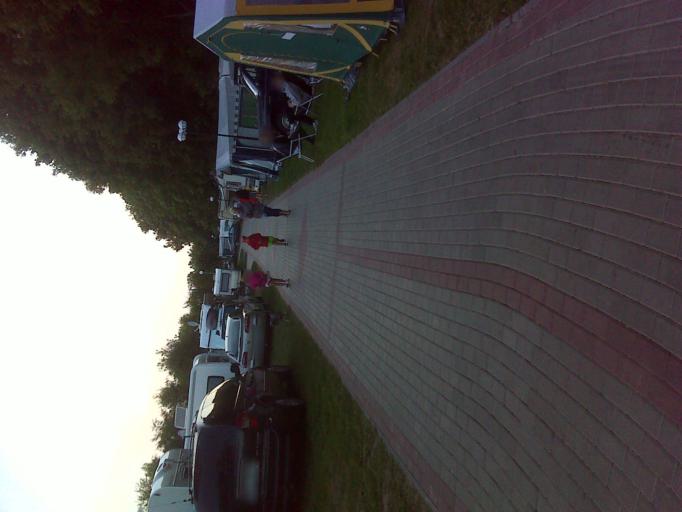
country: PL
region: West Pomeranian Voivodeship
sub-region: Powiat gryficki
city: Rewal
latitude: 54.0801
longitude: 15.0037
